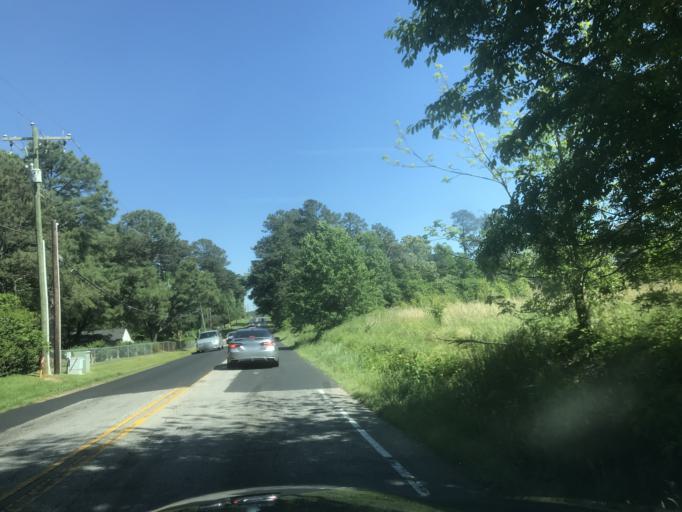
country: US
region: North Carolina
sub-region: Wake County
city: Raleigh
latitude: 35.7399
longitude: -78.6686
